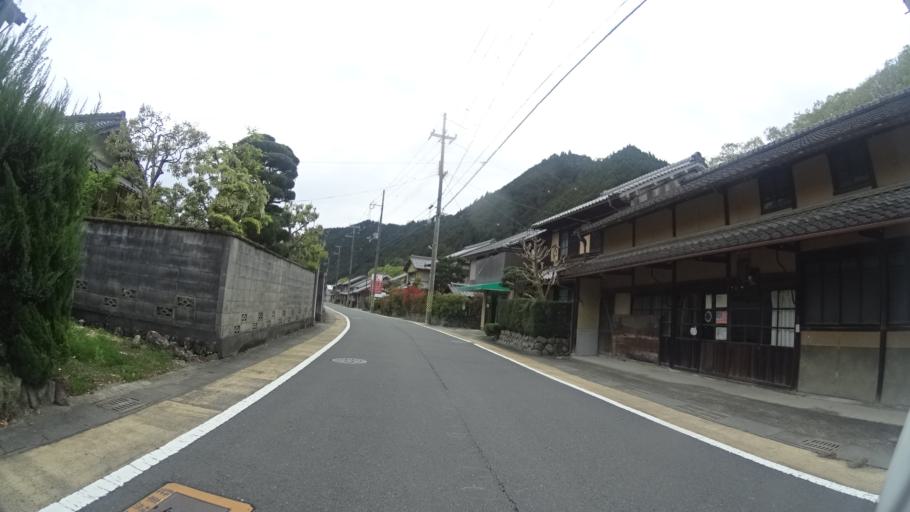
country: JP
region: Kyoto
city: Kameoka
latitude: 35.1560
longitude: 135.5042
